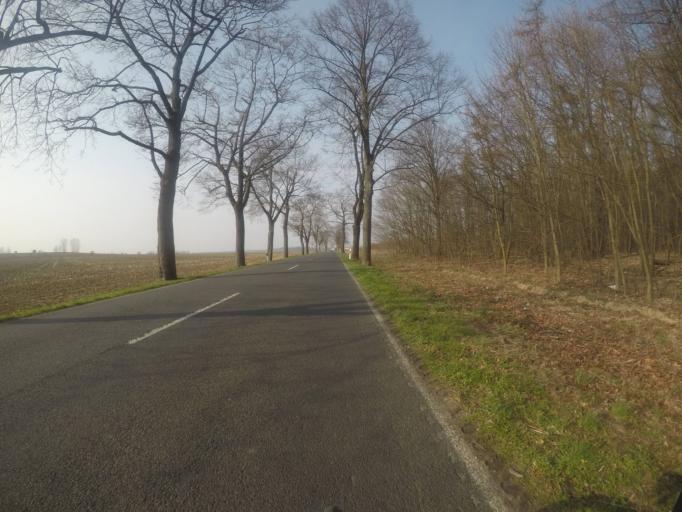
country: DE
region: Brandenburg
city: Schonefeld
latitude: 52.3432
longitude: 13.4868
